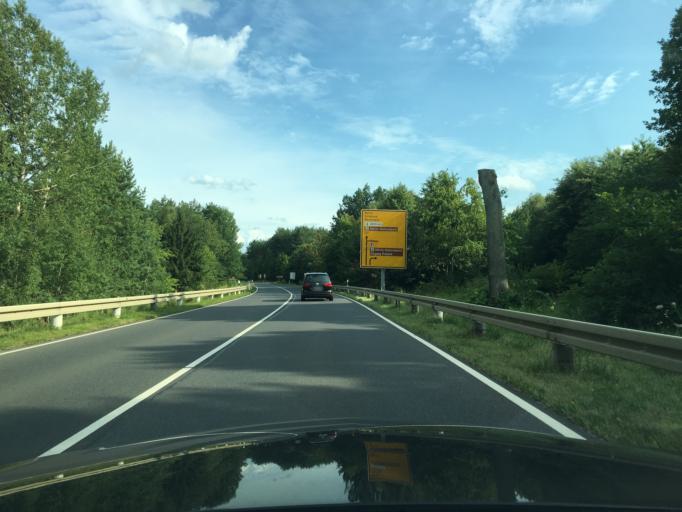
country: DE
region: Mecklenburg-Vorpommern
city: Neustrelitz
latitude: 53.3866
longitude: 13.0477
